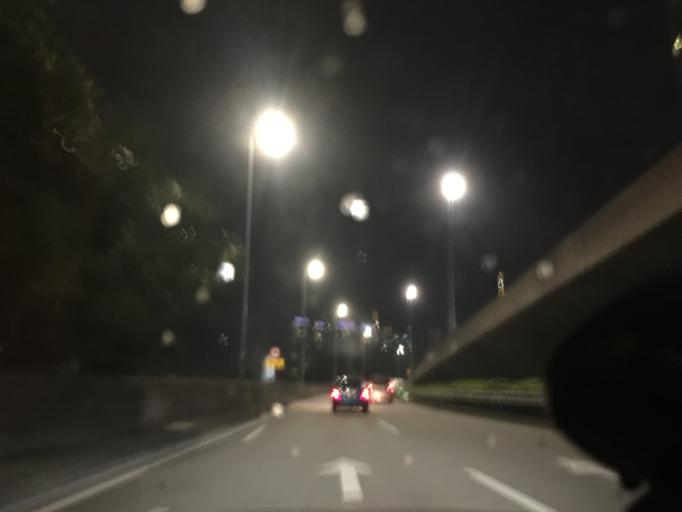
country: MY
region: Kuala Lumpur
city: Kuala Lumpur
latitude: 3.1590
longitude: 101.7031
